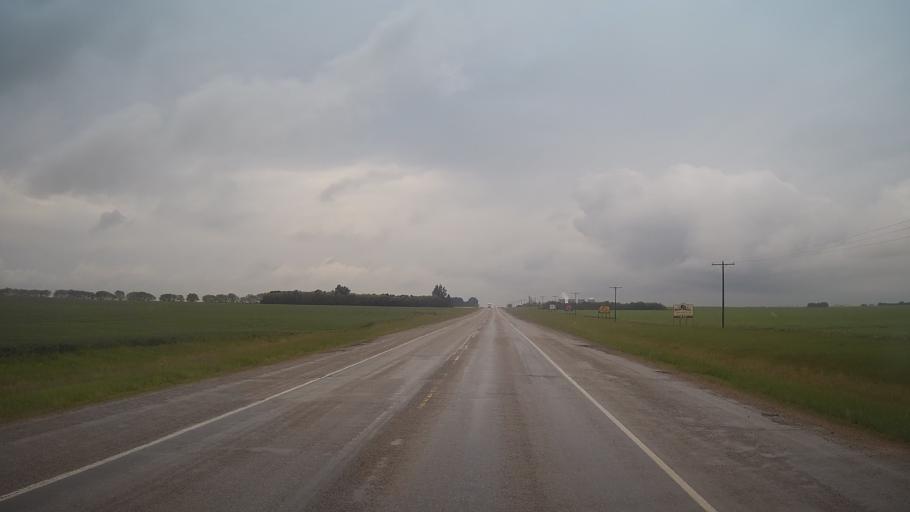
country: CA
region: Saskatchewan
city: Unity
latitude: 52.4349
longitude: -109.0762
